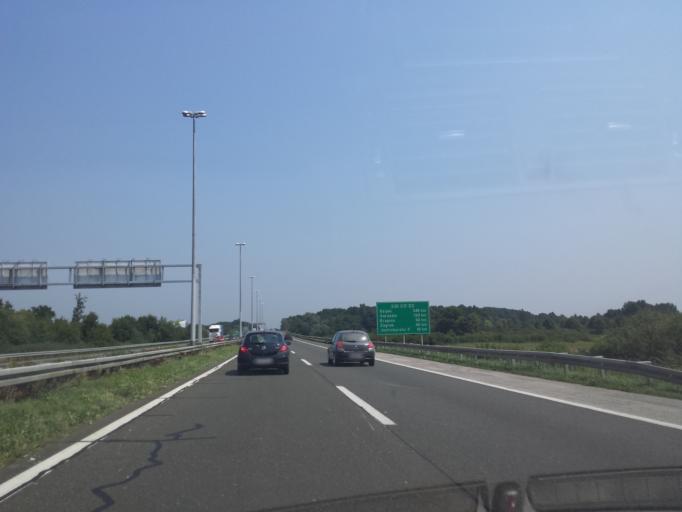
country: HR
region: Karlovacka
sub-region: Grad Karlovac
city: Karlovac
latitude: 45.5201
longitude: 15.5581
